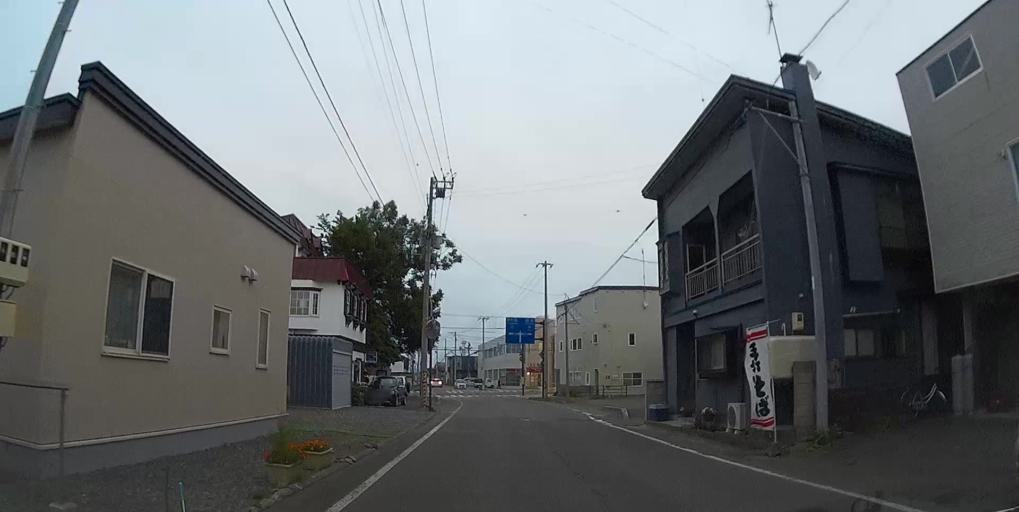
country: JP
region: Hokkaido
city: Nanae
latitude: 42.2568
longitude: 140.2677
